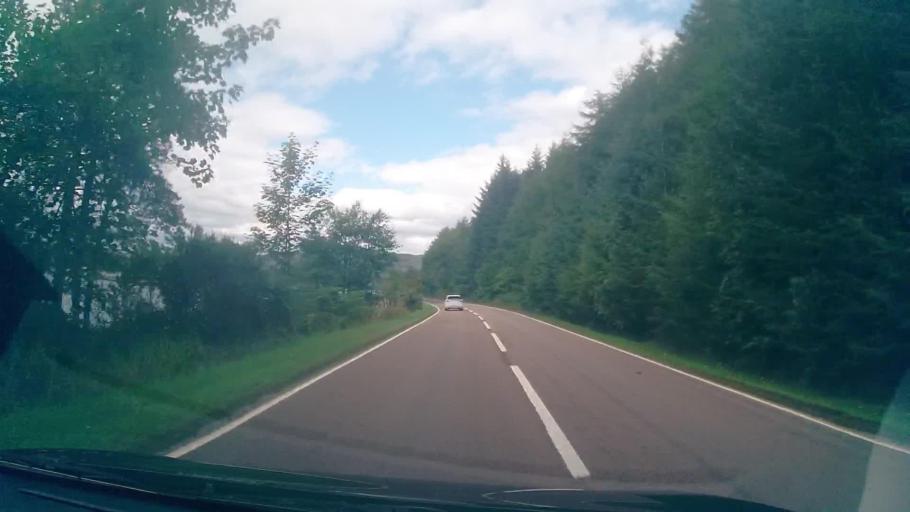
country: GB
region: Scotland
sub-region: Argyll and Bute
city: Oban
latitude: 56.4564
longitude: -5.3571
